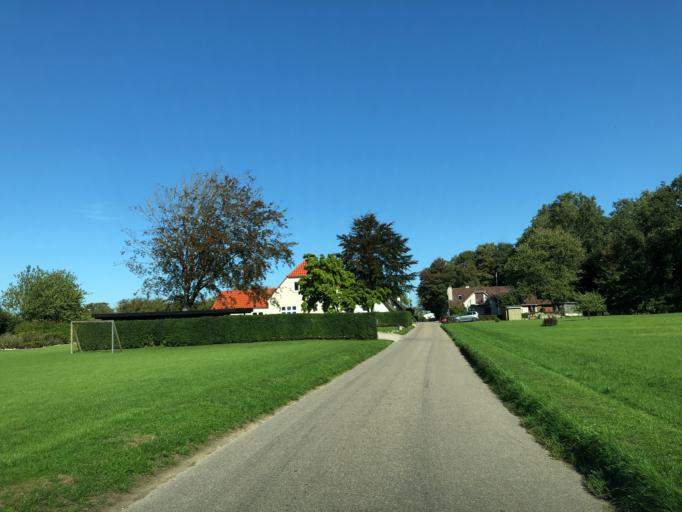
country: DK
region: South Denmark
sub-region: Sonderborg Kommune
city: Dybbol
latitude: 54.9681
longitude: 9.7358
